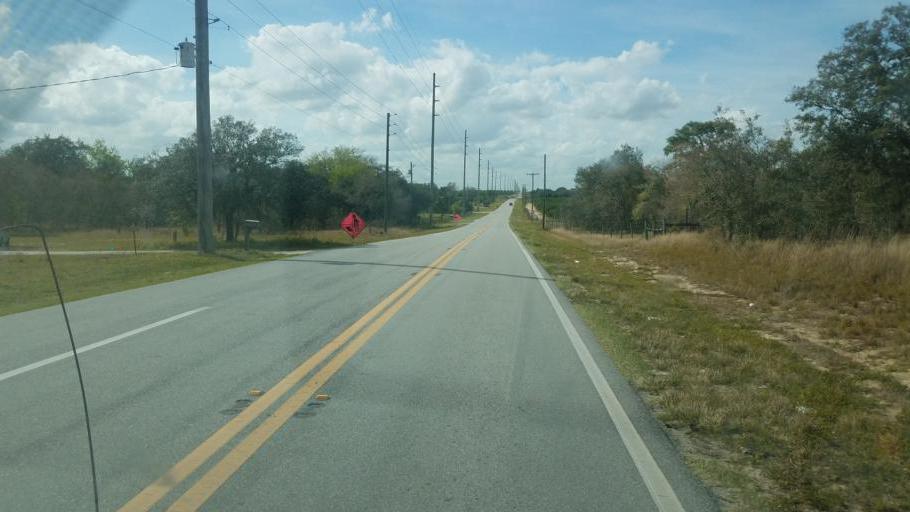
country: US
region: Florida
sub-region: Polk County
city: Lake Wales
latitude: 27.9612
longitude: -81.5525
